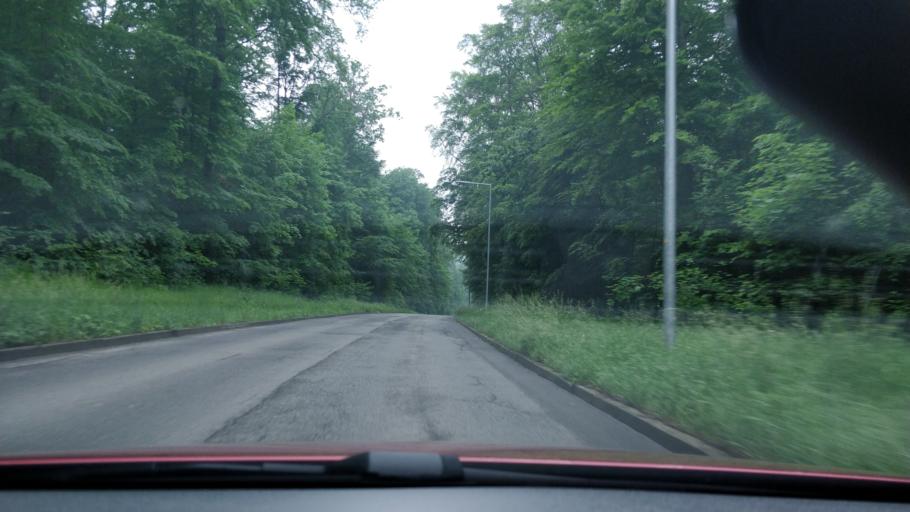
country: DE
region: Baden-Wuerttemberg
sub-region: Regierungsbezirk Stuttgart
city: Leinfelden-Echterdingen
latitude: 48.7266
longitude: 9.1839
